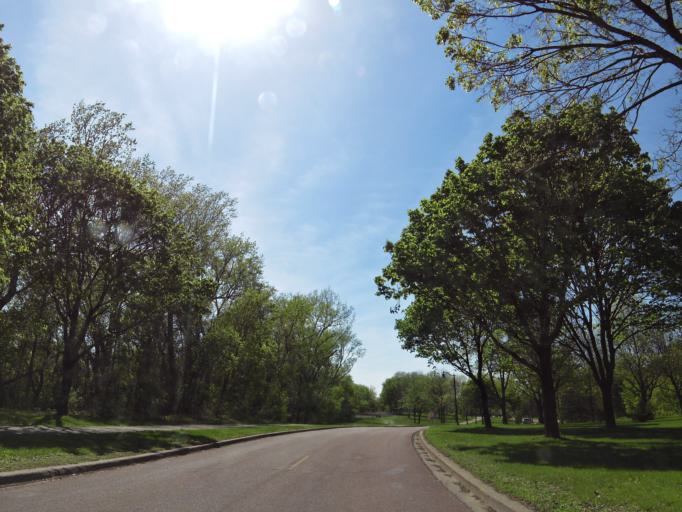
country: US
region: Minnesota
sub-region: Anoka County
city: Columbia Heights
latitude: 45.0242
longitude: -93.2513
